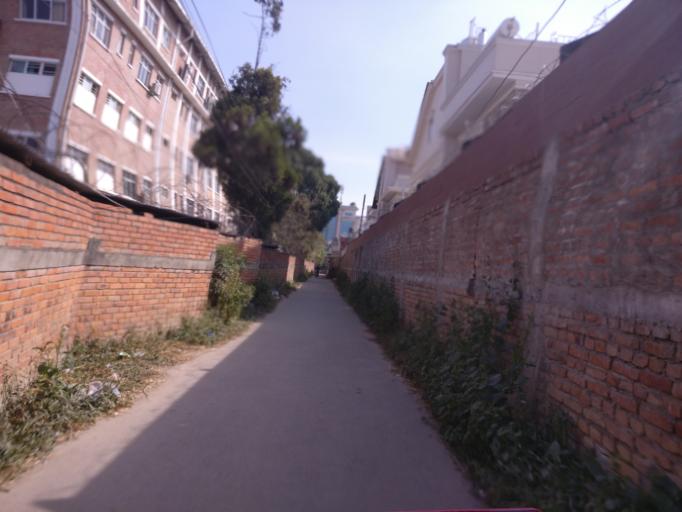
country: NP
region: Central Region
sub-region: Bagmati Zone
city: Patan
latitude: 27.6682
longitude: 85.3194
